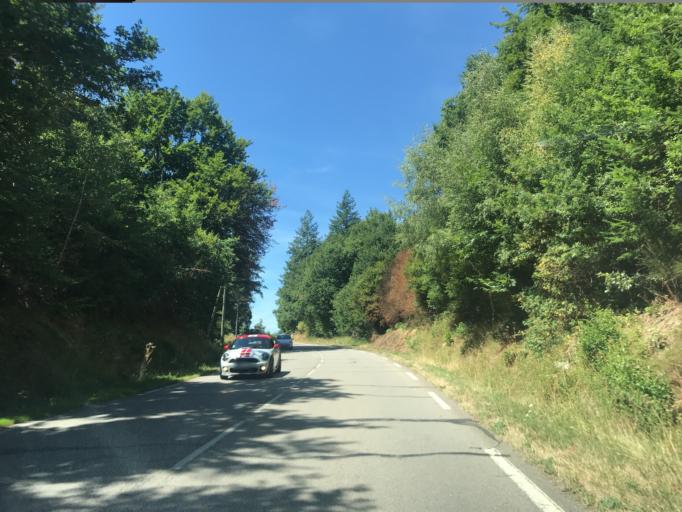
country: FR
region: Limousin
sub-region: Departement de la Correze
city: Meymac
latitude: 45.5206
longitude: 2.1688
